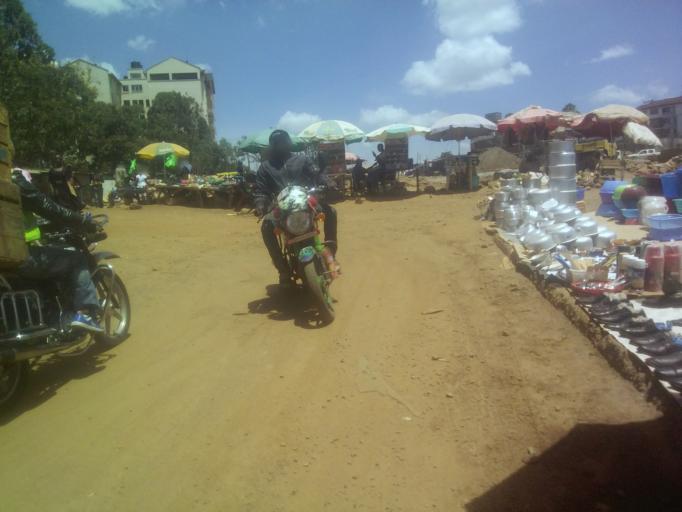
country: KE
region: Nairobi Area
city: Nairobi
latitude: -1.3048
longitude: 36.7880
